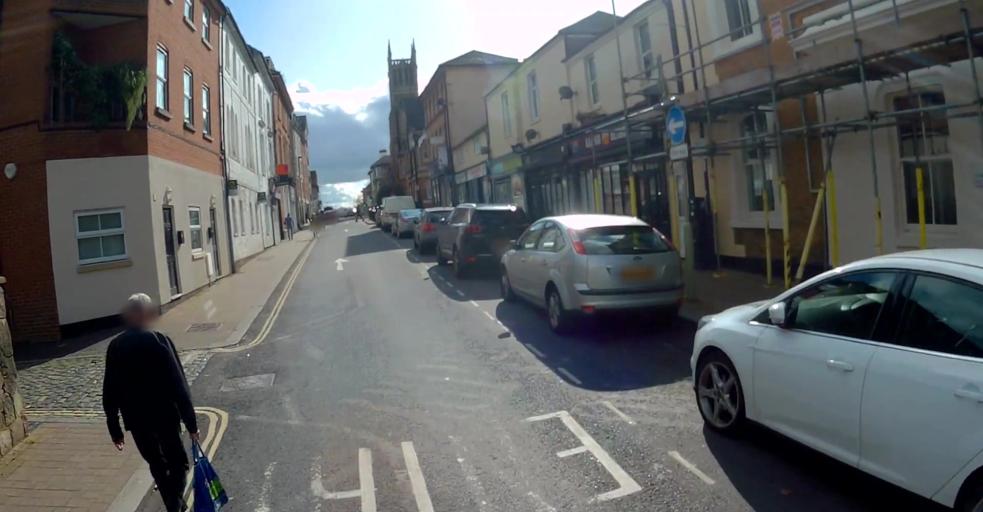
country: GB
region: England
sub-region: Hampshire
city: Aldershot
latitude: 51.2495
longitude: -0.7678
